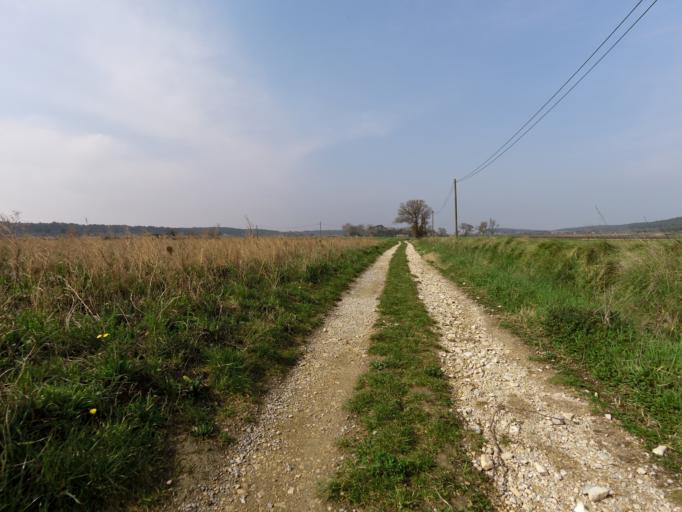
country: FR
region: Languedoc-Roussillon
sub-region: Departement du Gard
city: Calvisson
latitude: 43.7716
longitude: 4.1931
